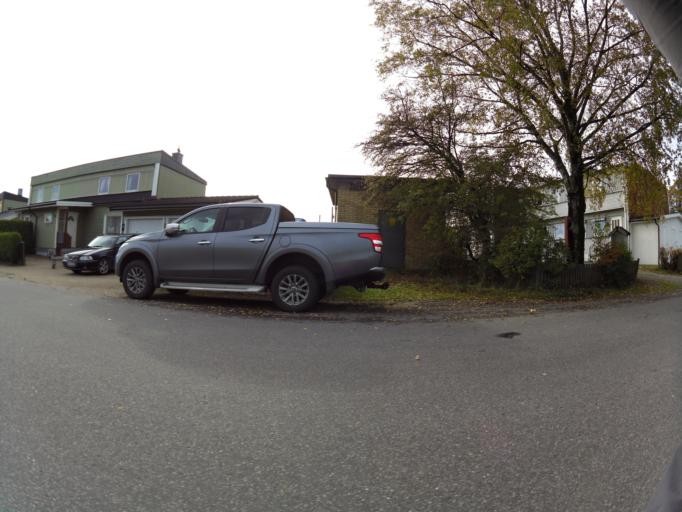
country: NO
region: Ostfold
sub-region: Fredrikstad
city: Fredrikstad
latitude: 59.2204
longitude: 10.9096
